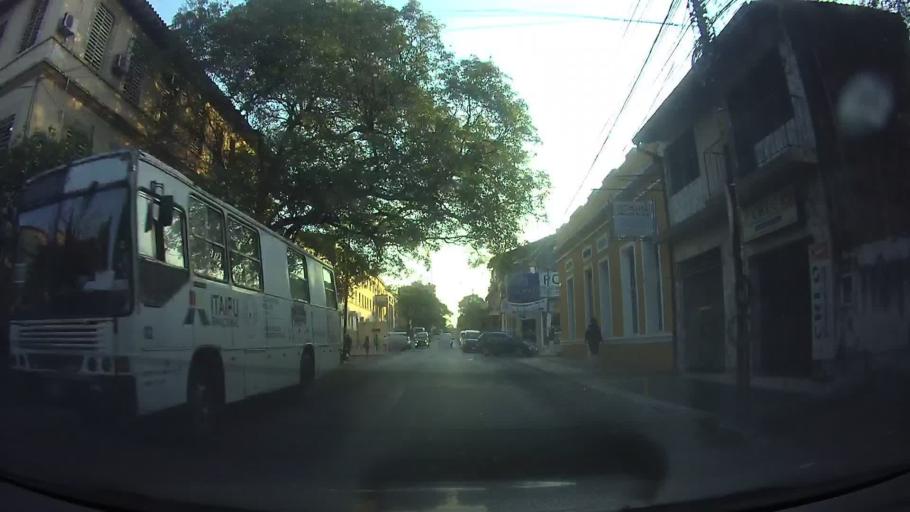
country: PY
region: Asuncion
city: Asuncion
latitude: -25.2916
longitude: -57.6267
